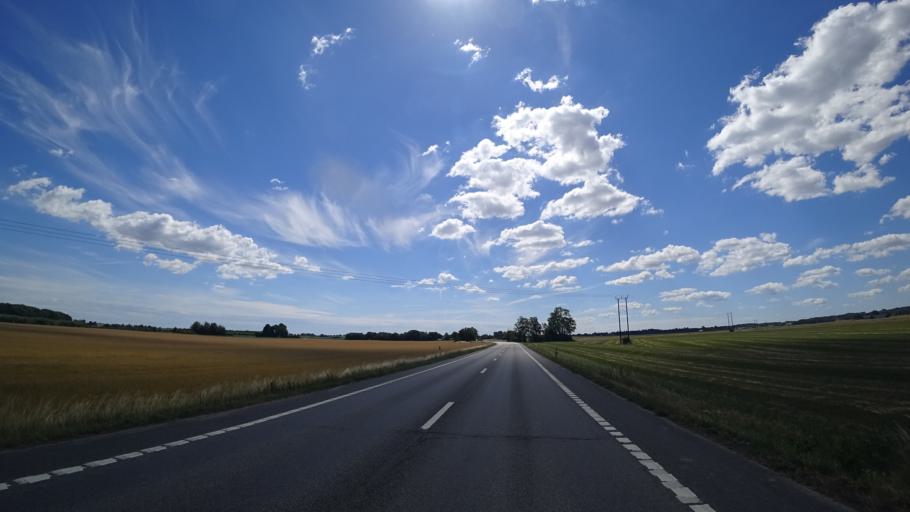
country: SE
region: Skane
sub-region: Kristianstads Kommun
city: Kristianstad
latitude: 56.0331
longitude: 14.0967
